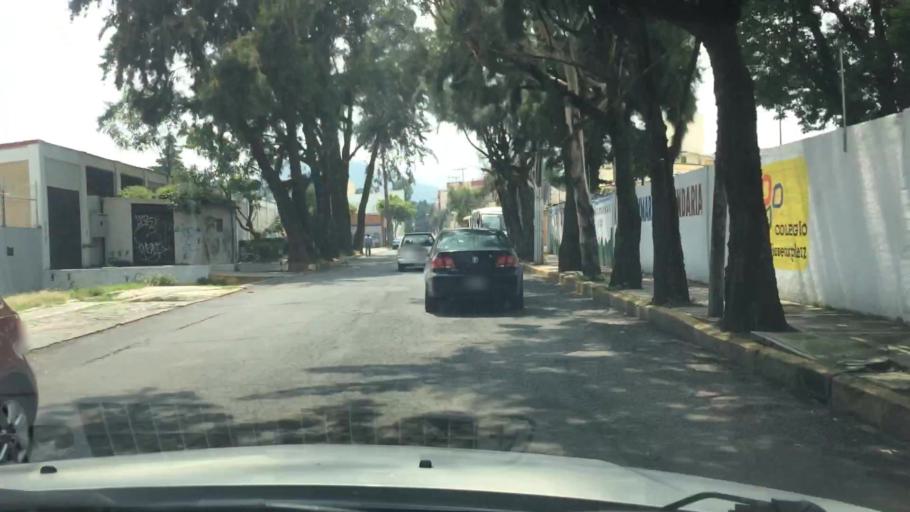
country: MX
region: Mexico City
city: Xochimilco
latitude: 19.2760
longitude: -99.1290
